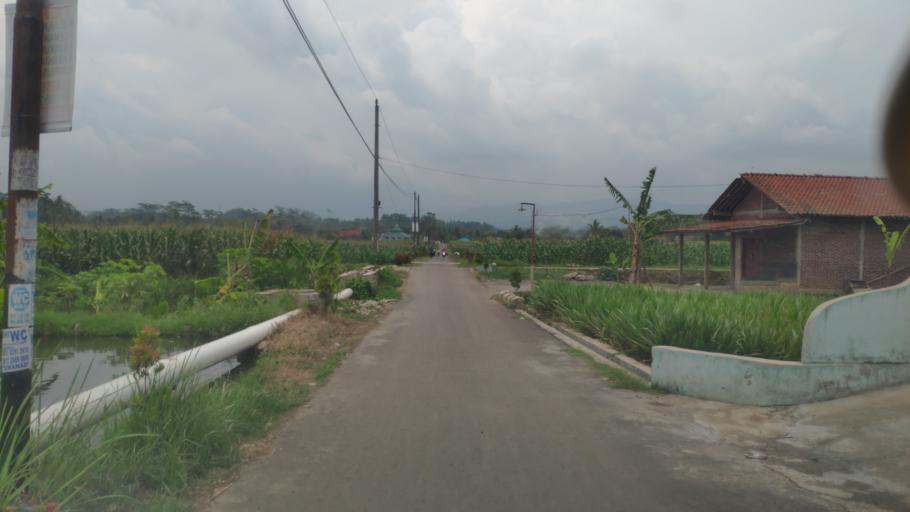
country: ID
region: Central Java
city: Gombong
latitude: -7.4064
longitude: 109.6025
